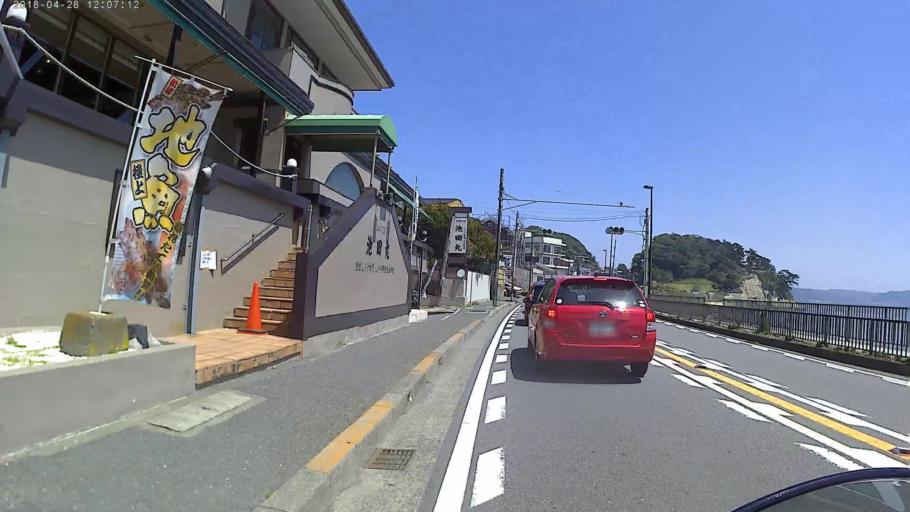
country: JP
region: Kanagawa
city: Kamakura
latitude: 35.3034
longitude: 139.5210
